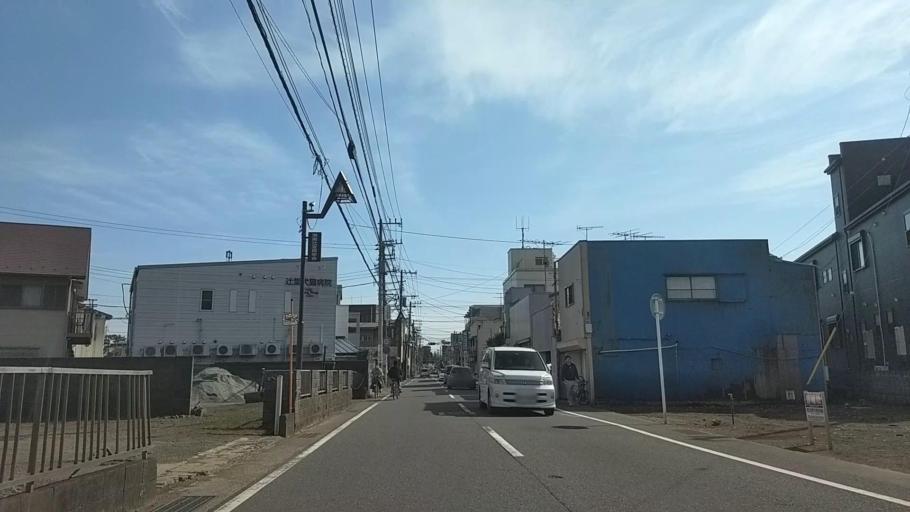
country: JP
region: Kanagawa
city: Fujisawa
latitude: 35.3310
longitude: 139.4513
